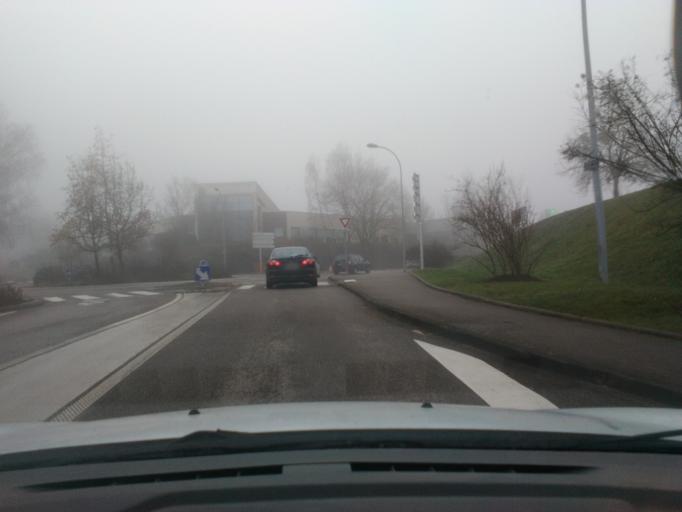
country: FR
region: Lorraine
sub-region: Departement des Vosges
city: Epinal
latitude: 48.1881
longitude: 6.4641
